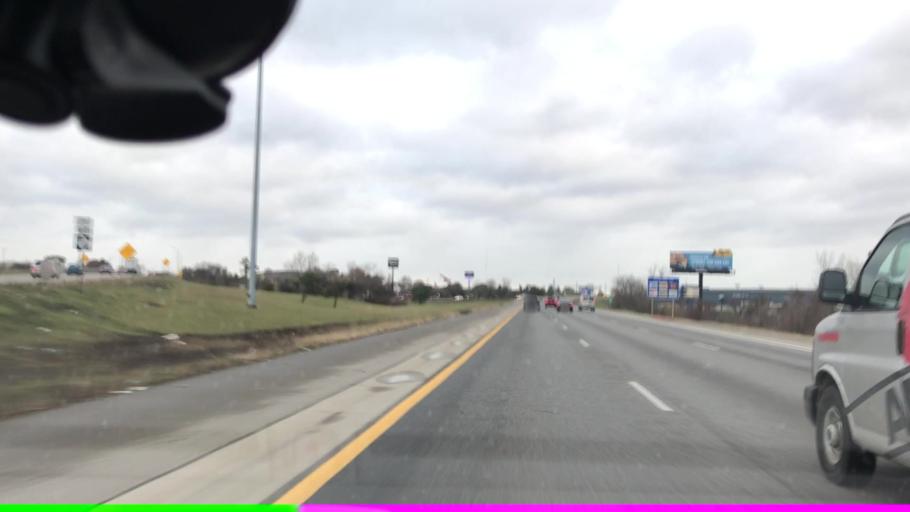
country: US
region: Michigan
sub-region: Macomb County
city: Roseville
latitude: 42.5197
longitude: -82.9165
